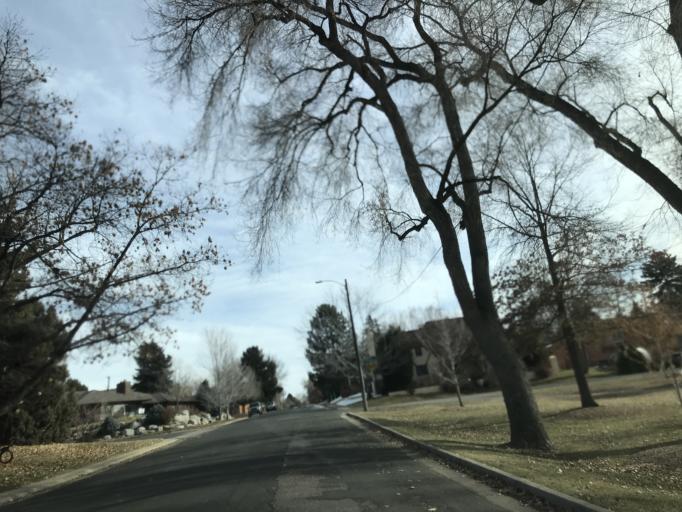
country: US
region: Colorado
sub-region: Arapahoe County
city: Littleton
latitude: 39.6111
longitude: -105.0109
